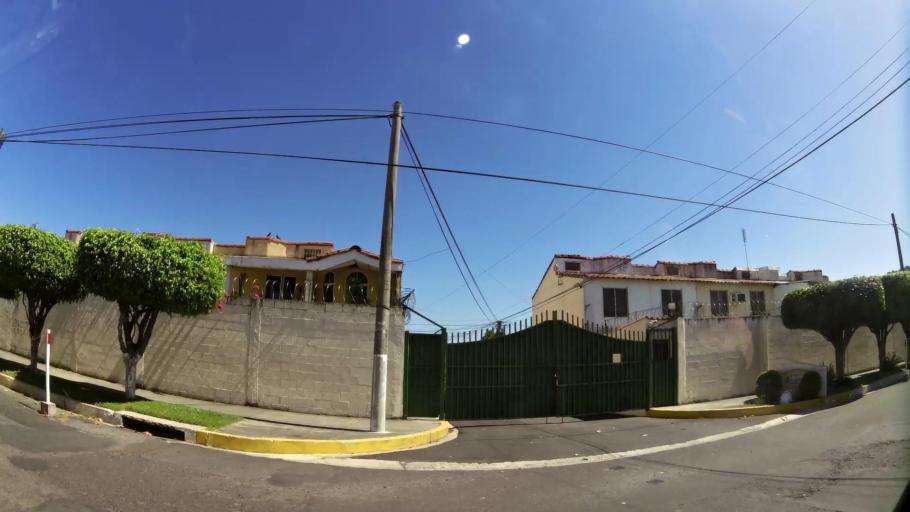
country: SV
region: La Libertad
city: Santa Tecla
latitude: 13.6691
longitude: -89.2764
